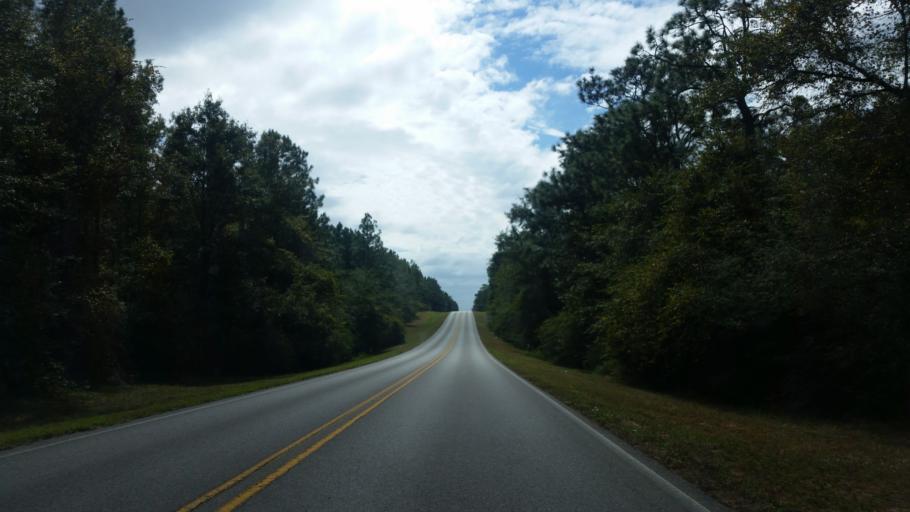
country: US
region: Florida
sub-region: Santa Rosa County
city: Point Baker
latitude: 30.7394
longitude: -86.9479
